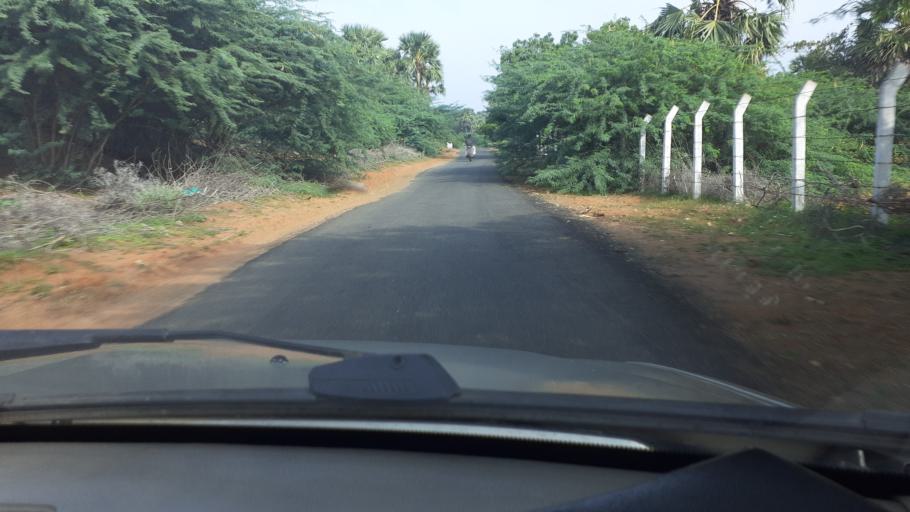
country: IN
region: Tamil Nadu
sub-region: Tirunelveli Kattabo
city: Tisaiyanvilai
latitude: 8.3377
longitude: 77.9436
